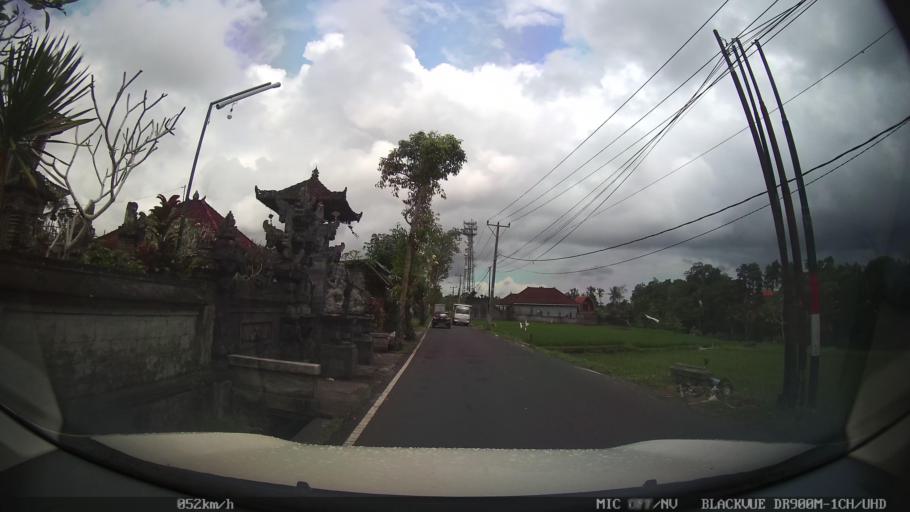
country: ID
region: Bali
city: Banjar Pekenjelodan
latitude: -8.5616
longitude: 115.1781
